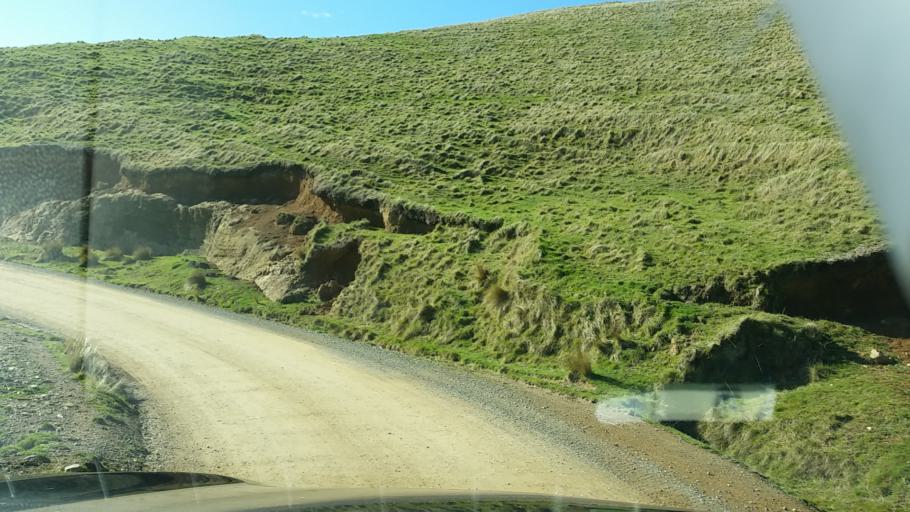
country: NZ
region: Marlborough
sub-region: Marlborough District
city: Picton
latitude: -40.9515
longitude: 173.8330
